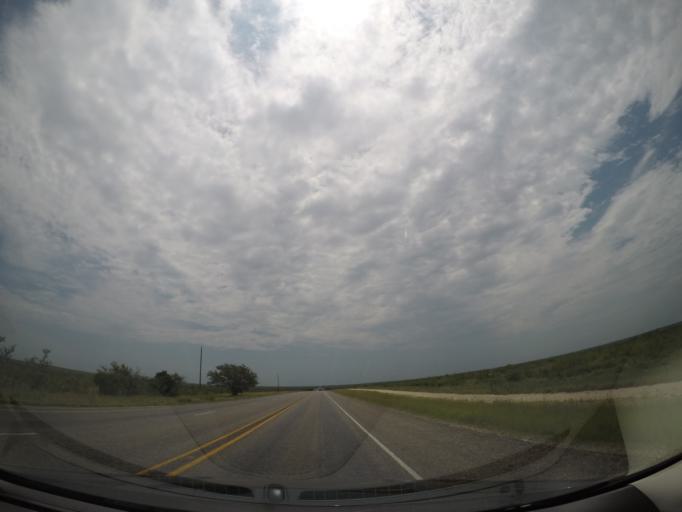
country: US
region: Texas
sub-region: Kinney County
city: Fort Clark Springs
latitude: 29.3263
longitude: -100.4808
